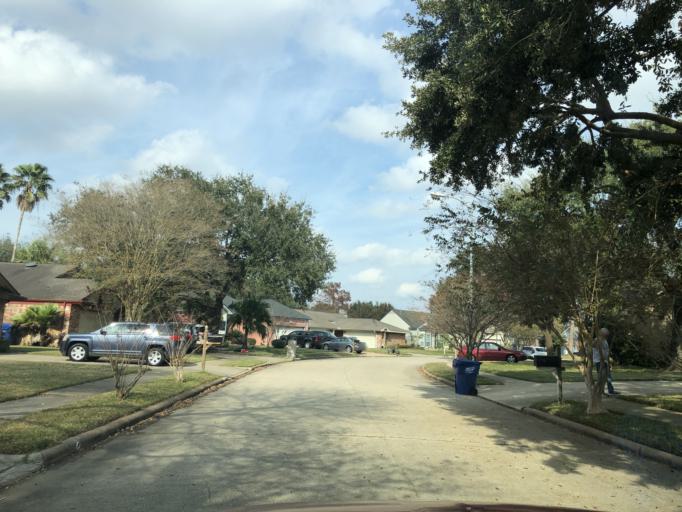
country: US
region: Texas
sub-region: Harris County
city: Tomball
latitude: 30.0383
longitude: -95.5434
